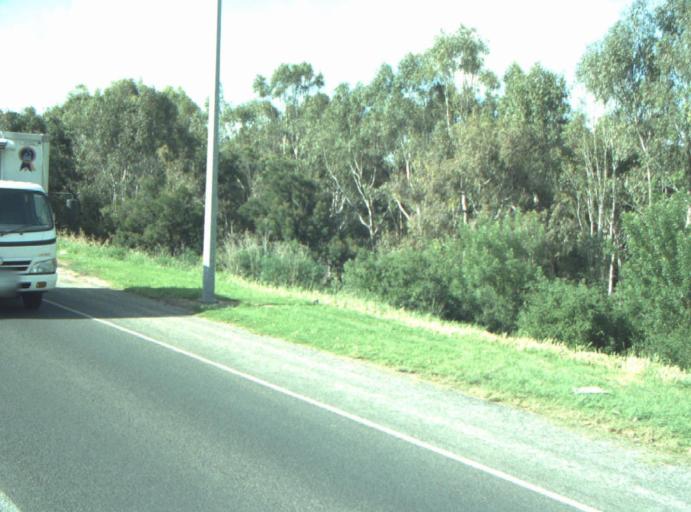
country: AU
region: Victoria
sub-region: Greater Geelong
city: Wandana Heights
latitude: -38.1656
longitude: 144.3295
